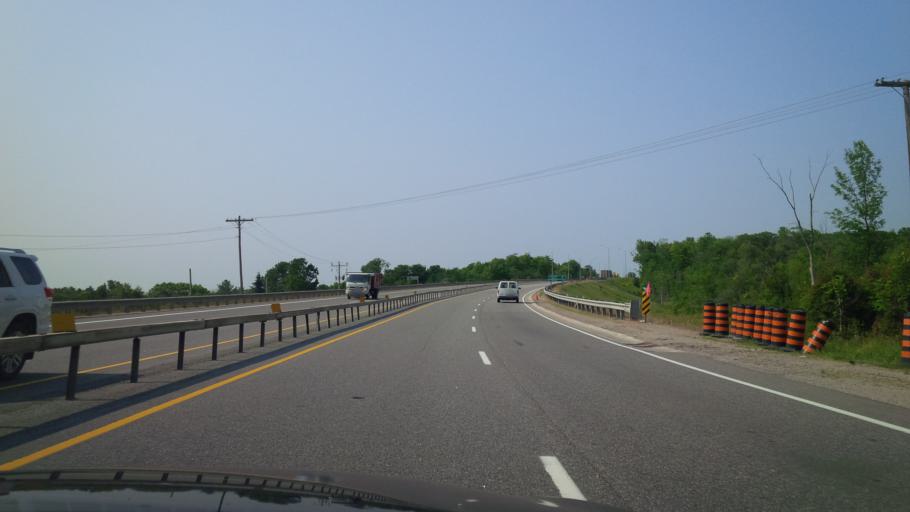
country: CA
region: Ontario
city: Orillia
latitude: 44.6479
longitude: -79.4187
